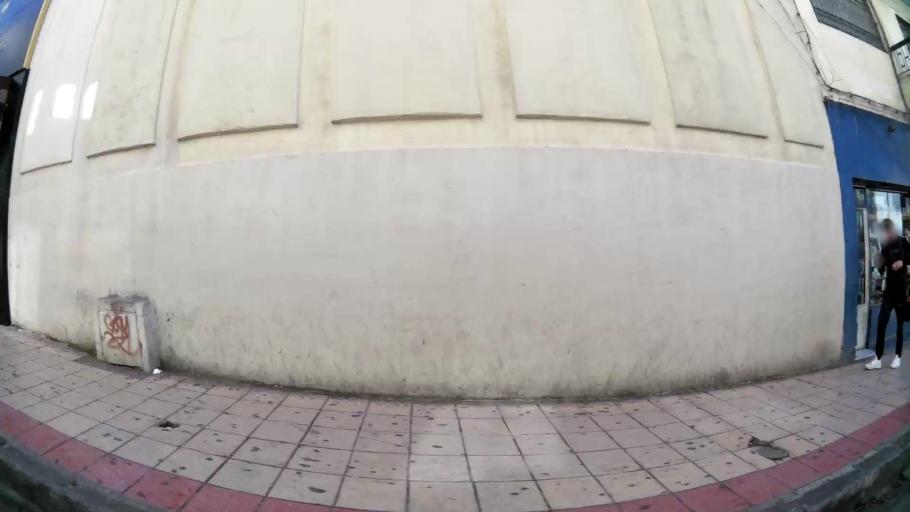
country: MA
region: Tanger-Tetouan
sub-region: Tanger-Assilah
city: Tangier
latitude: 35.7795
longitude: -5.8181
